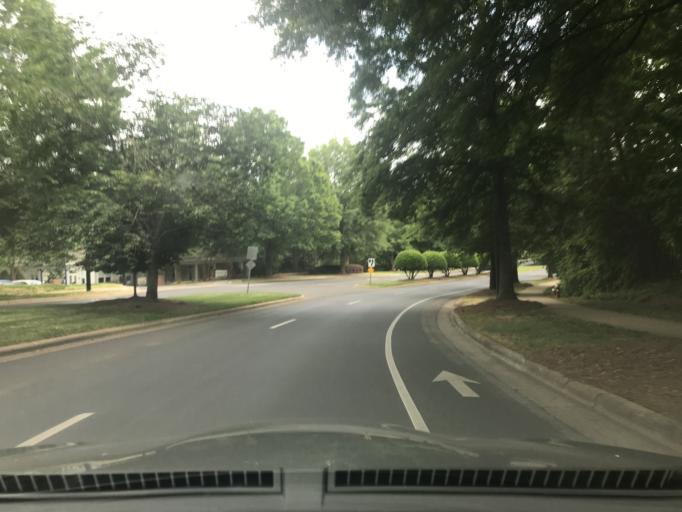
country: US
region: North Carolina
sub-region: Wake County
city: Wake Forest
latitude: 35.9100
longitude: -78.5870
